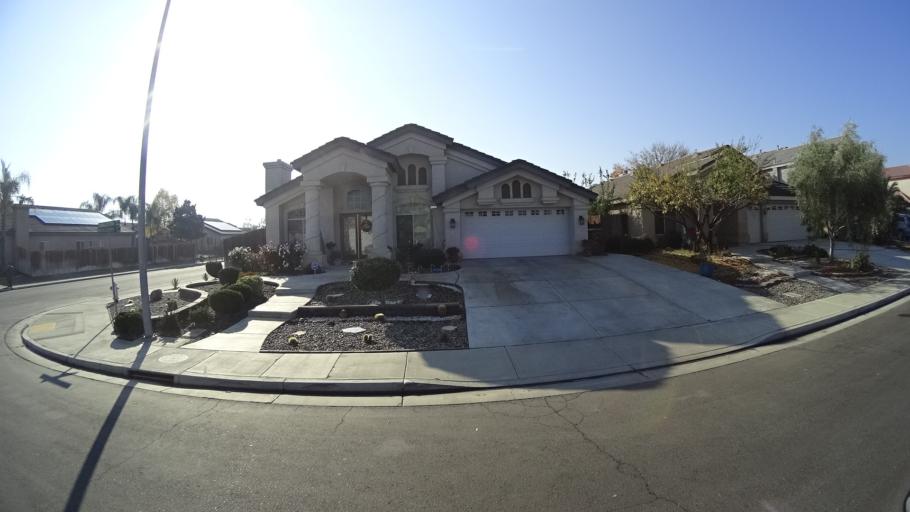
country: US
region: California
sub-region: Kern County
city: Greenacres
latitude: 35.3082
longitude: -119.1152
